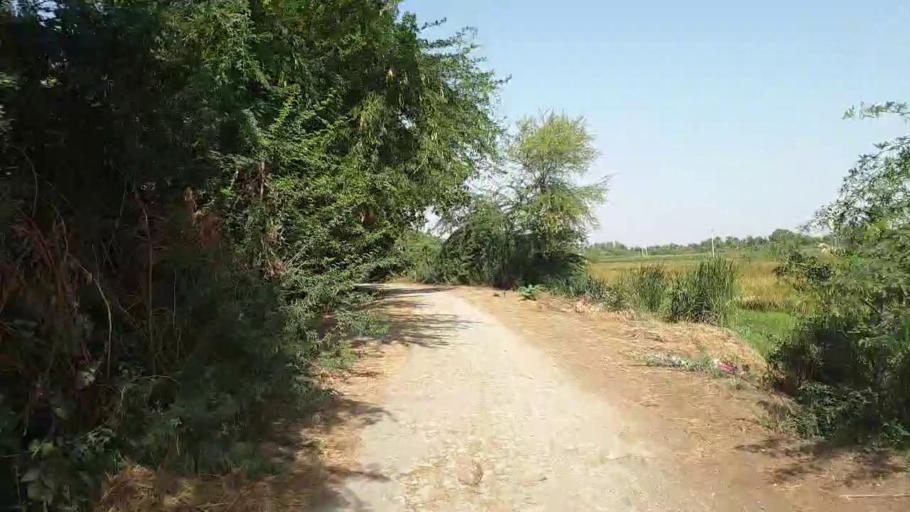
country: PK
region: Sindh
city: Tando Bago
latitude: 24.7621
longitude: 69.0236
